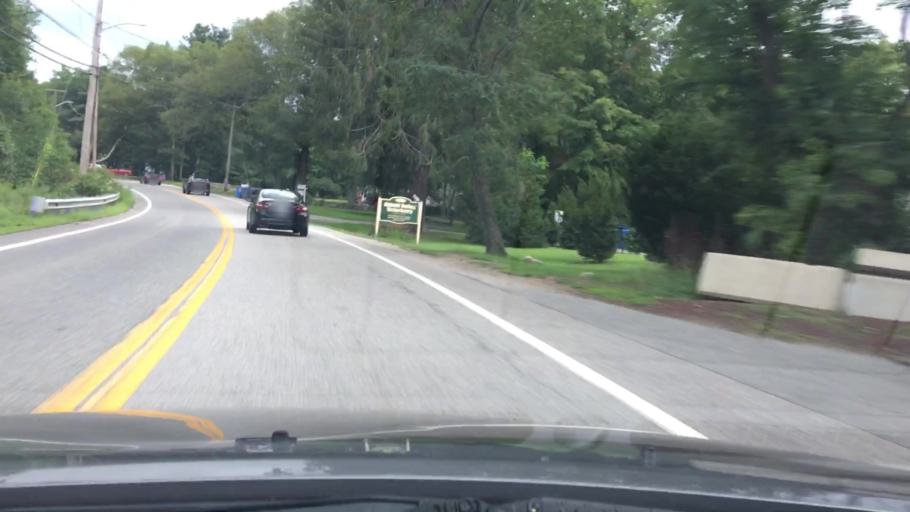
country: US
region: Rhode Island
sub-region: Providence County
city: Cumberland
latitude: 42.0020
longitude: -71.4195
